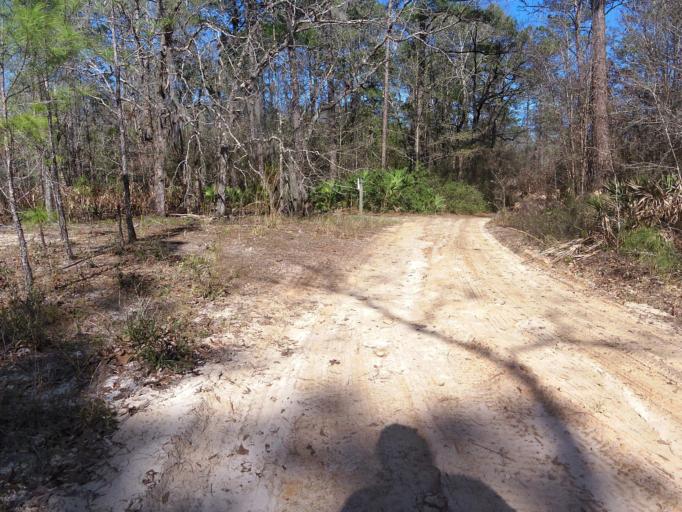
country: US
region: Florida
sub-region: Clay County
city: Middleburg
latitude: 30.1367
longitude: -81.8878
